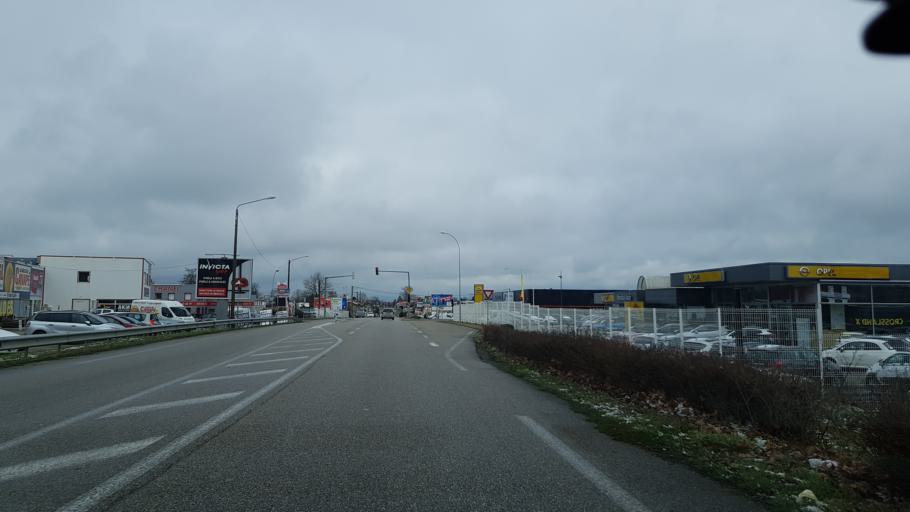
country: FR
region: Rhone-Alpes
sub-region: Departement de l'Ain
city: Peronnas
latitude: 46.1703
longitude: 5.1962
